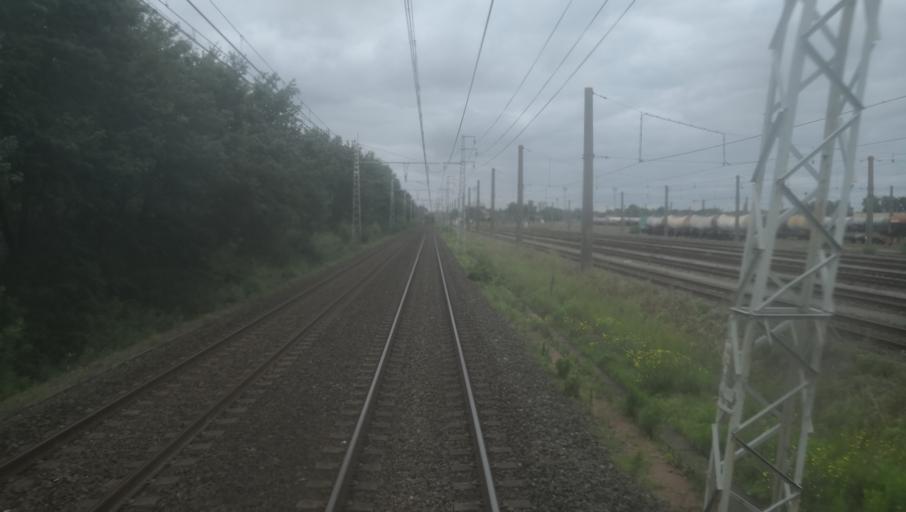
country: FR
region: Midi-Pyrenees
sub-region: Departement de la Haute-Garonne
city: Lespinasse
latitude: 43.7026
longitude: 1.3908
